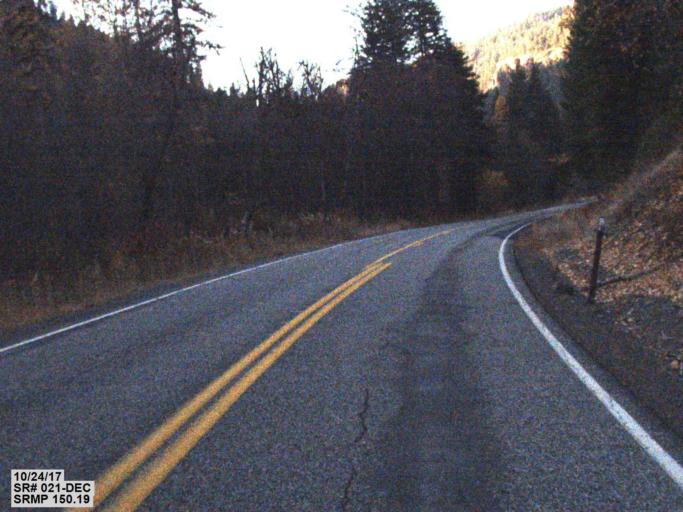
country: US
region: Washington
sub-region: Ferry County
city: Republic
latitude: 48.5077
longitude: -118.7380
